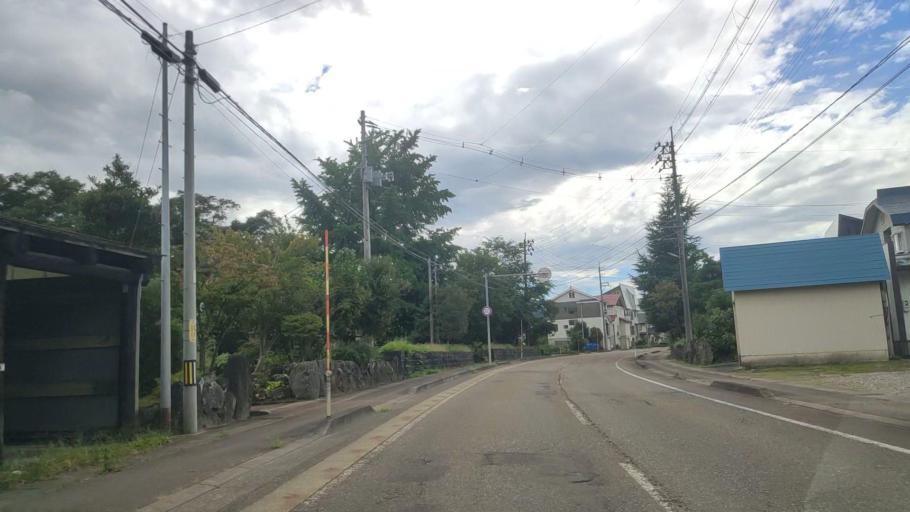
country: JP
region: Niigata
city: Arai
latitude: 36.9856
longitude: 138.2722
